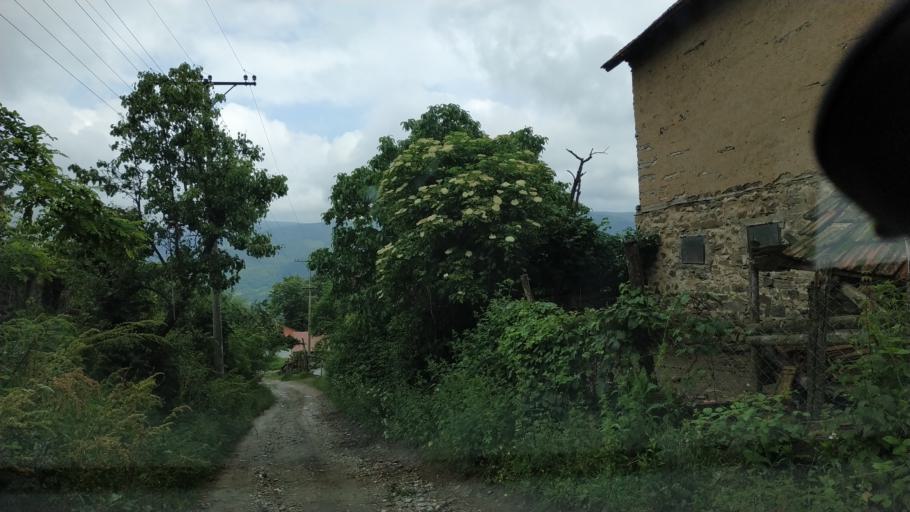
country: RS
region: Central Serbia
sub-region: Toplicki Okrug
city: Prokuplje
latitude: 43.4005
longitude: 21.5485
